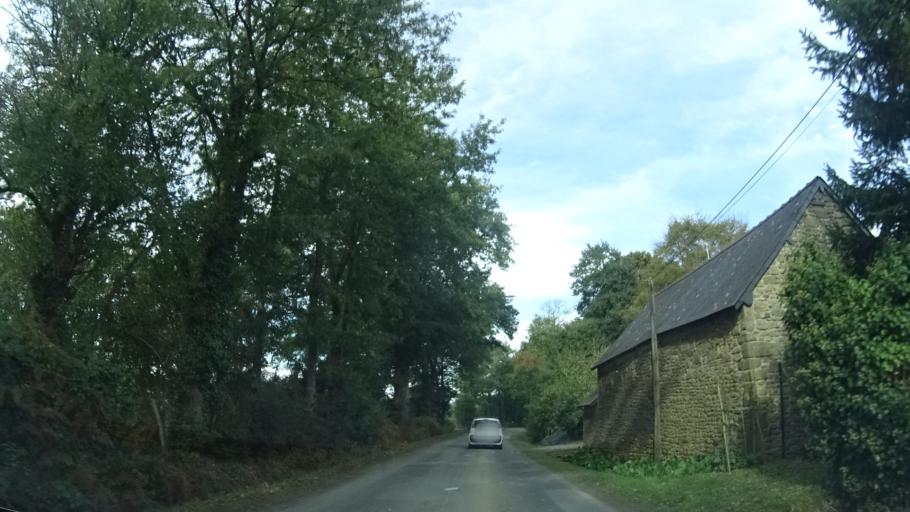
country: FR
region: Brittany
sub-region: Departement d'Ille-et-Vilaine
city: Bonnemain
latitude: 48.4500
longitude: -1.7983
